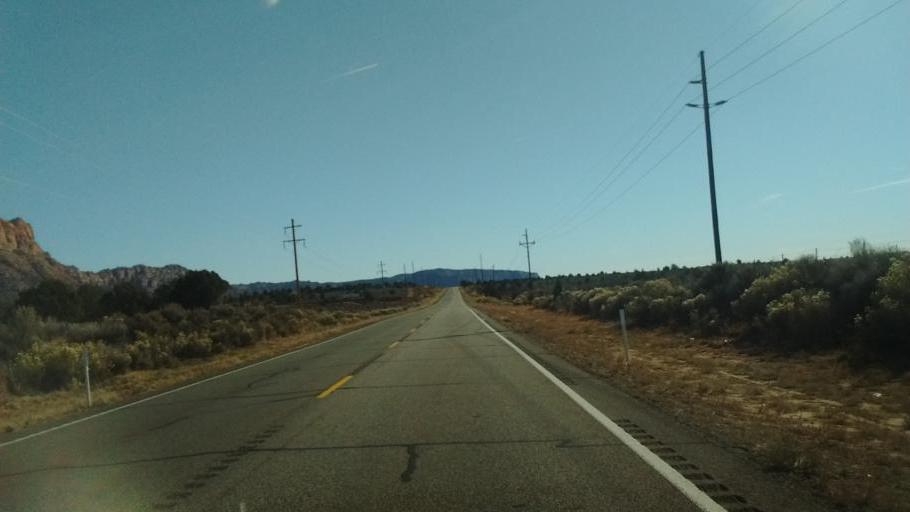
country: US
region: Arizona
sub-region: Mohave County
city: Colorado City
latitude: 37.0255
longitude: -113.0461
